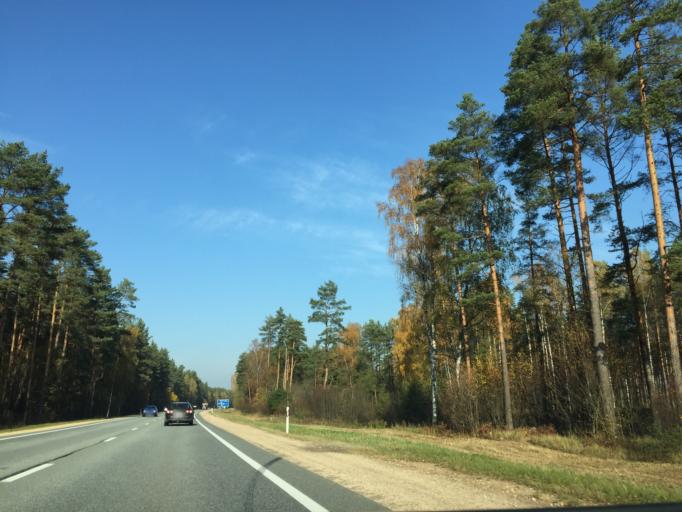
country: LV
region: Babite
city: Pinki
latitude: 56.9110
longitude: 23.9159
